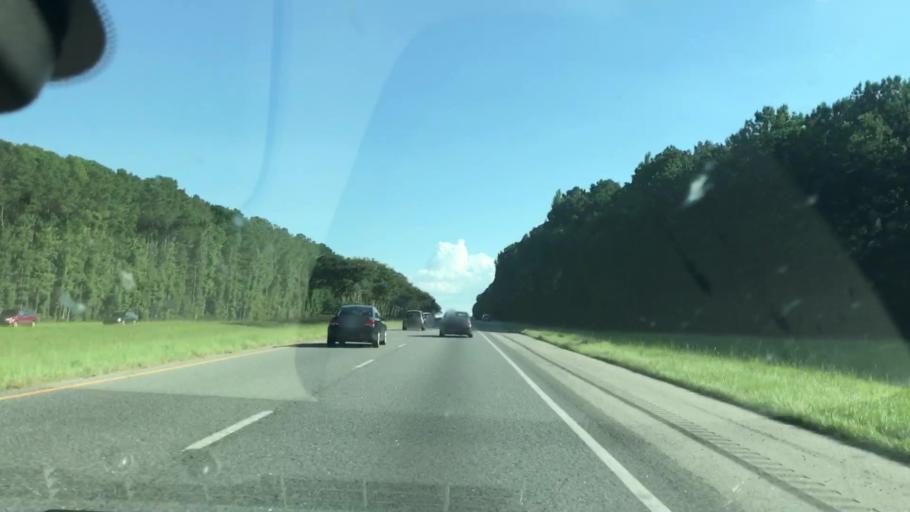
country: US
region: Georgia
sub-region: Harris County
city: Hamilton
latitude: 32.8119
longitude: -85.0214
